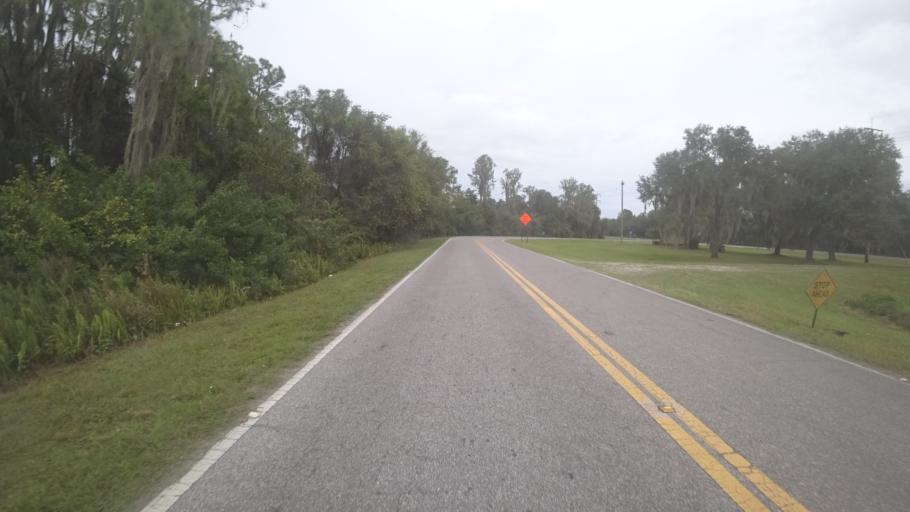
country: US
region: Florida
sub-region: Hardee County
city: Bowling Green
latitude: 27.6481
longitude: -82.0542
